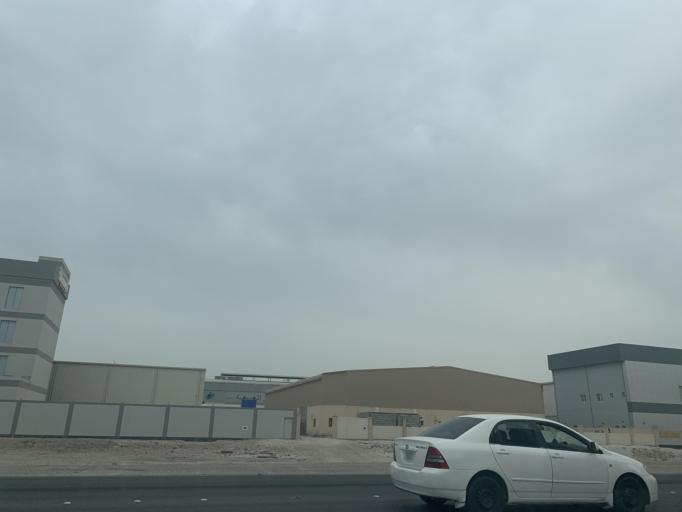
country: BH
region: Muharraq
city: Al Hadd
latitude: 26.2122
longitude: 50.6656
